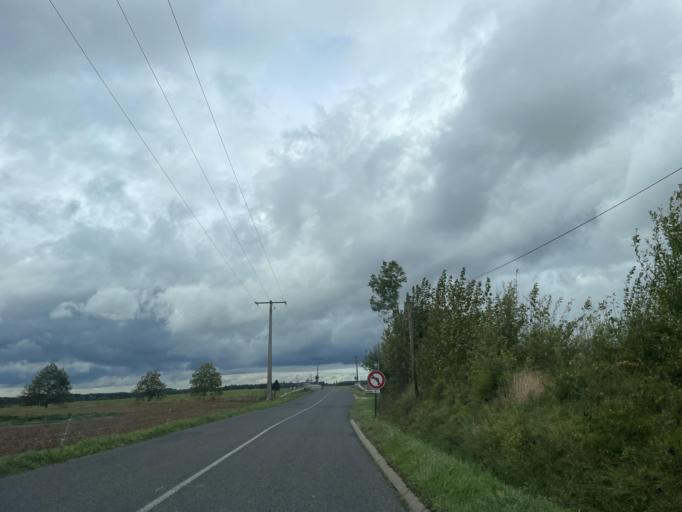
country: FR
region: Ile-de-France
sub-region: Departement de Seine-et-Marne
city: Saint-Jean-les-Deux-Jumeaux
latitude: 48.9224
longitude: 3.0054
